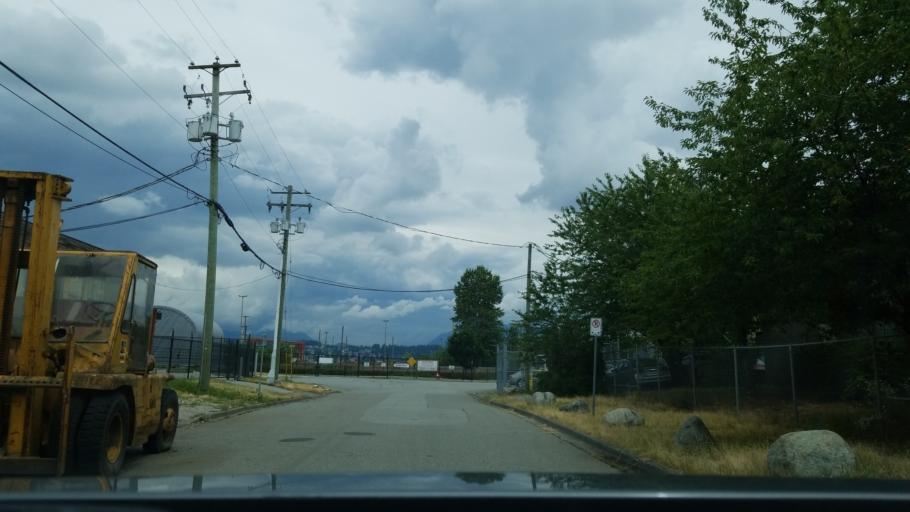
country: CA
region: British Columbia
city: New Westminster
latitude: 49.2123
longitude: -122.8550
